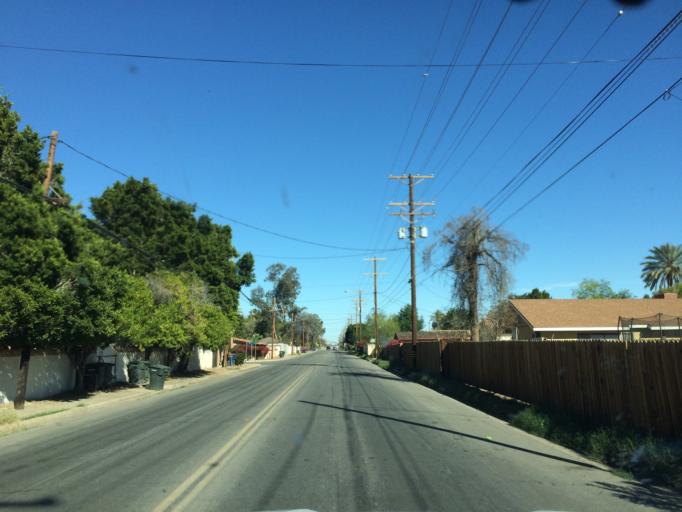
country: US
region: California
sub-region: Imperial County
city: El Centro
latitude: 32.7815
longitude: -115.5599
